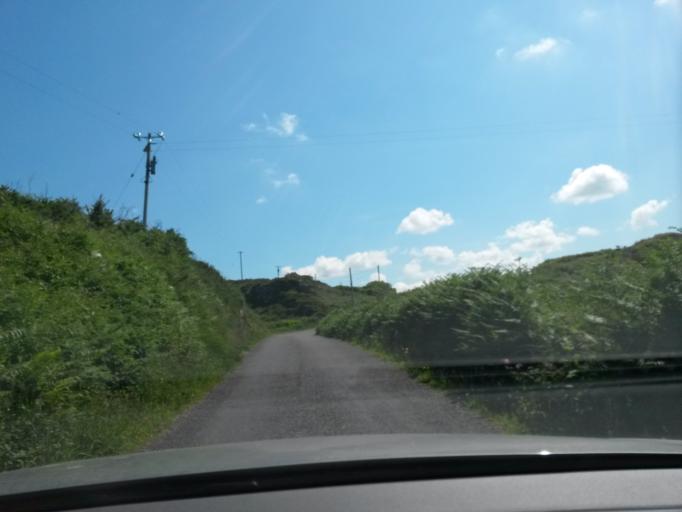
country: IE
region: Munster
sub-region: Ciarrai
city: Cahersiveen
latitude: 51.7174
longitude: -9.9781
